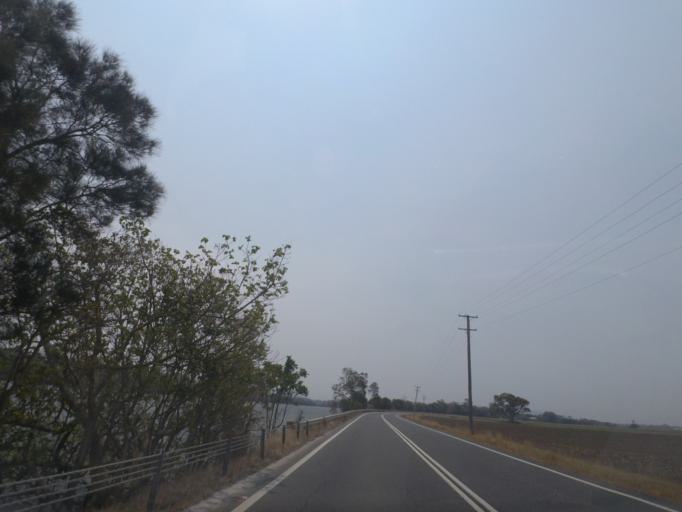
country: AU
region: New South Wales
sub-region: Richmond Valley
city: Evans Head
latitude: -28.9758
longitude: 153.4613
